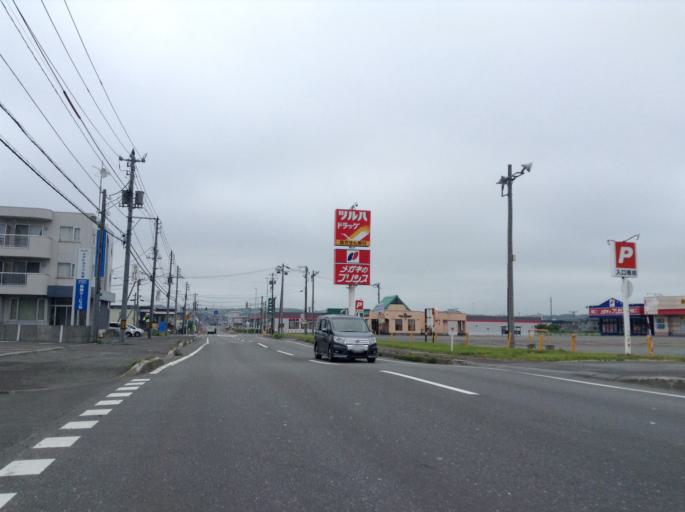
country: JP
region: Hokkaido
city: Wakkanai
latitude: 45.3865
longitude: 141.6977
